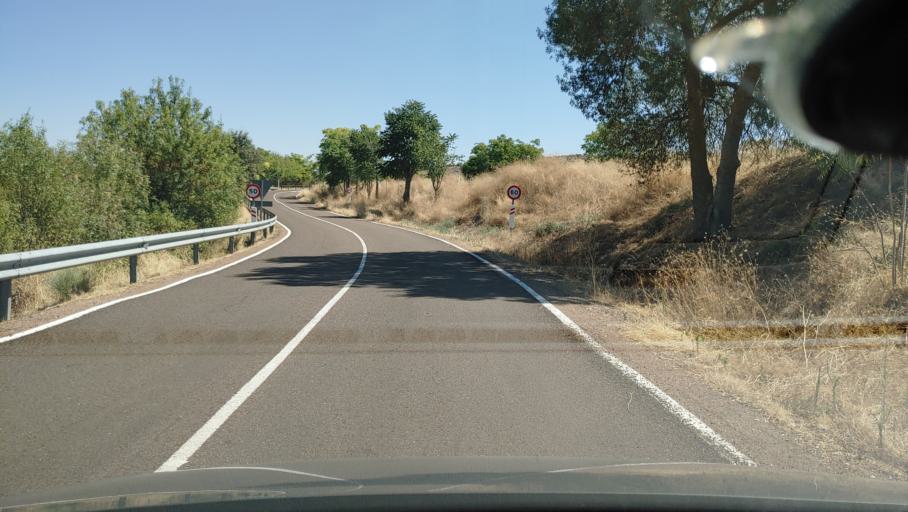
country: ES
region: Castille-La Mancha
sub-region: Provincia de Ciudad Real
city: Alamillo
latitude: 38.7408
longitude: -4.7288
